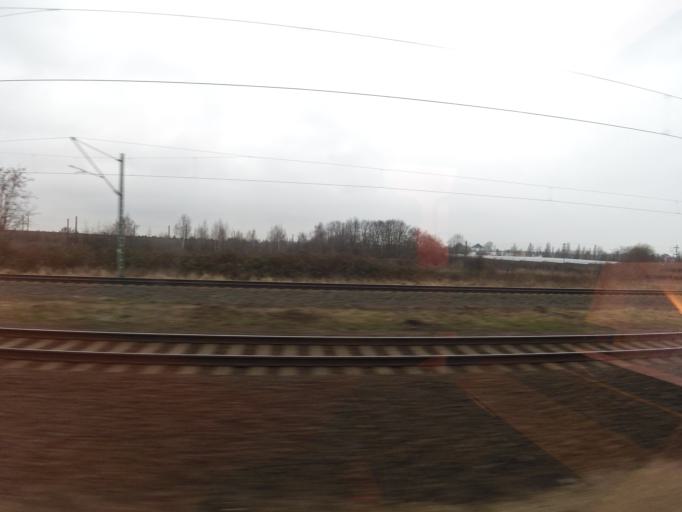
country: DE
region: Saxony
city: Rackwitz
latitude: 51.3936
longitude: 12.3903
